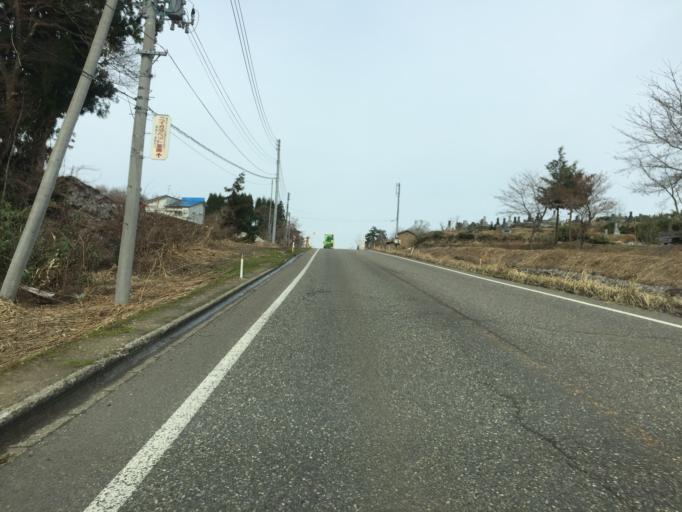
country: JP
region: Niigata
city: Tochio-honcho
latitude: 37.4498
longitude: 138.9515
